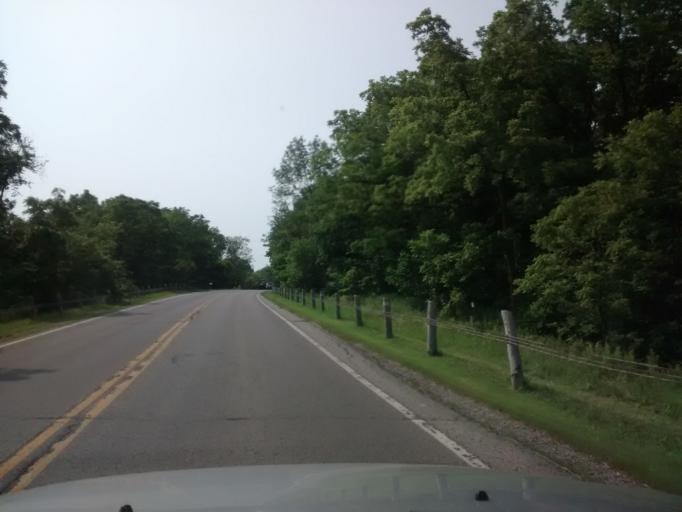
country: CA
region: Ontario
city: Ancaster
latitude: 43.0137
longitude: -79.8827
